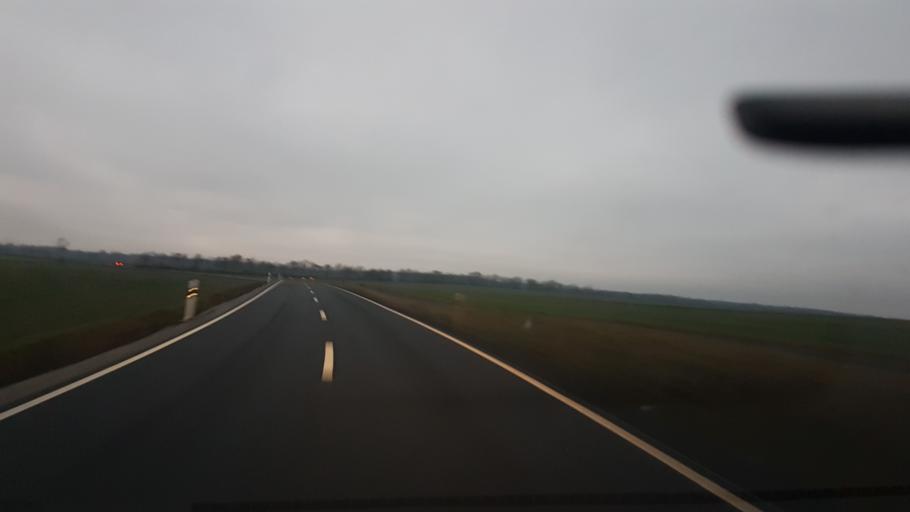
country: DE
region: Bavaria
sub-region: Regierungsbezirk Unterfranken
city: Ermershausen
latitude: 50.2144
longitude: 10.6194
